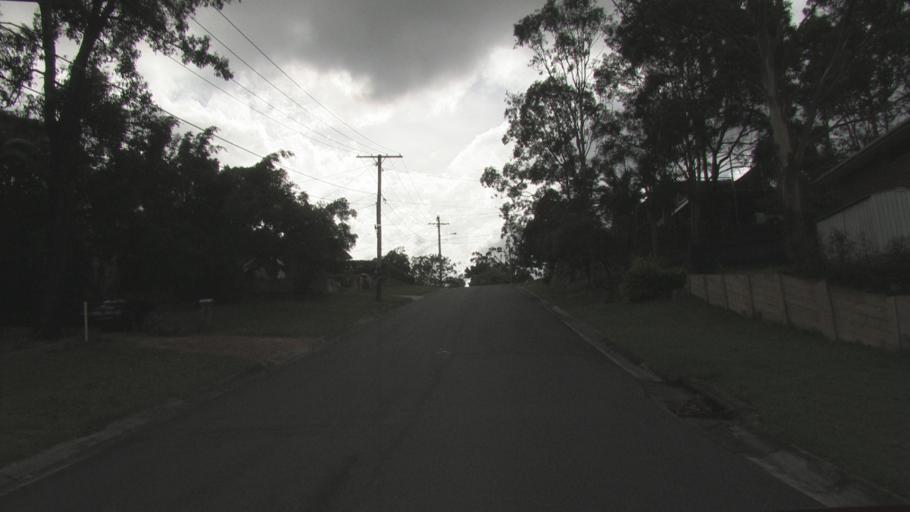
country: AU
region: Queensland
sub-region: Logan
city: Beenleigh
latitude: -27.6794
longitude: 153.2044
